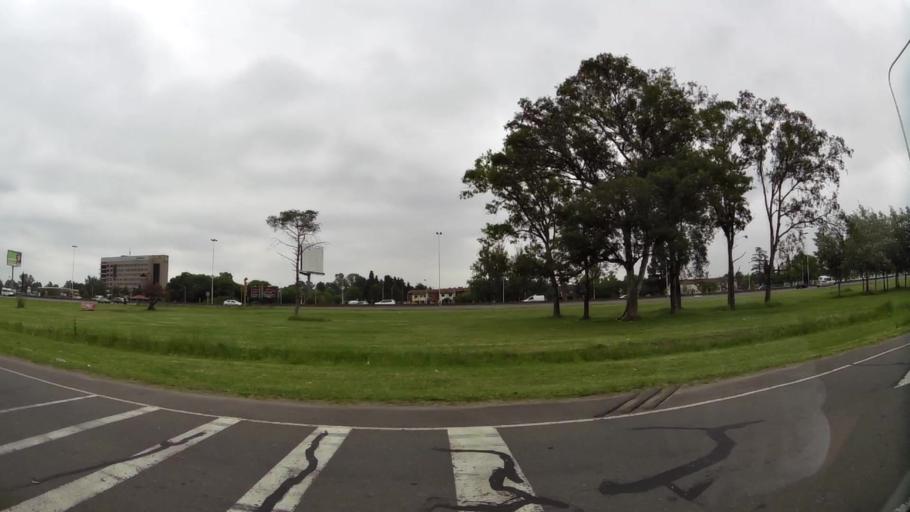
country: AR
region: Buenos Aires F.D.
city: Villa Lugano
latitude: -34.7327
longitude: -58.5168
